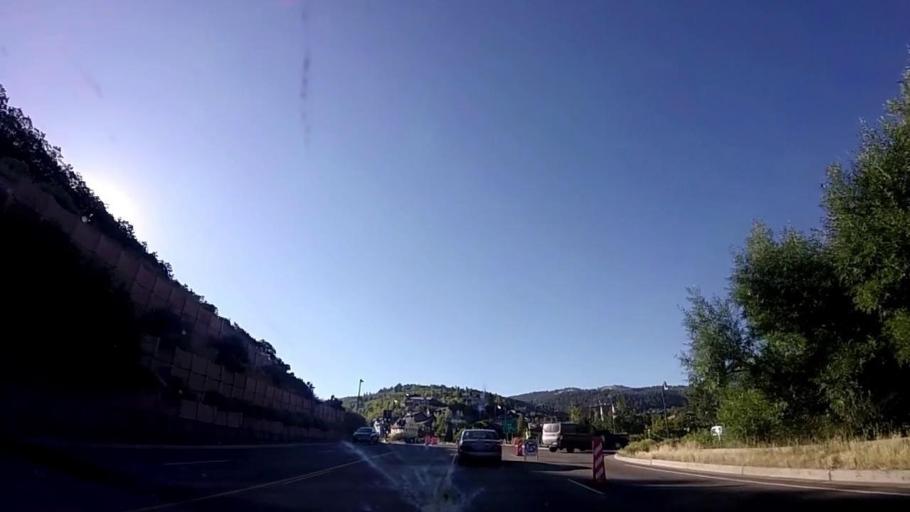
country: US
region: Utah
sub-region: Summit County
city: Park City
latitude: 40.6468
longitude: -111.4959
